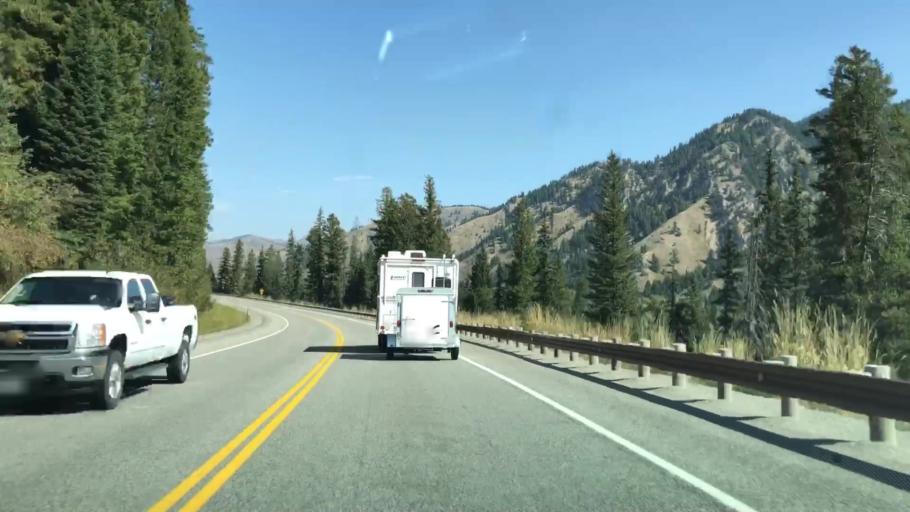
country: US
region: Wyoming
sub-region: Teton County
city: Hoback
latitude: 43.2433
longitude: -110.7762
